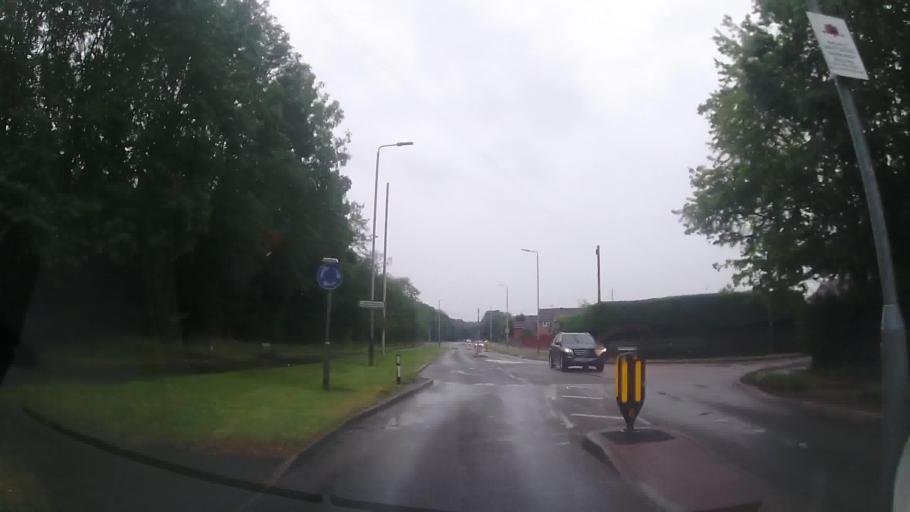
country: GB
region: England
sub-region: Leicestershire
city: Anstey
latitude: 52.6737
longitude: -1.1599
